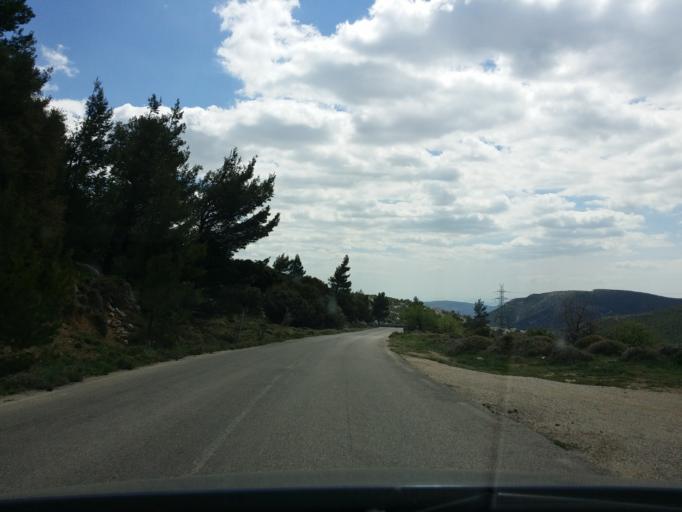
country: GR
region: Attica
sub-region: Nomarchia Dytikis Attikis
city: Fyli
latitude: 38.1438
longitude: 23.6452
